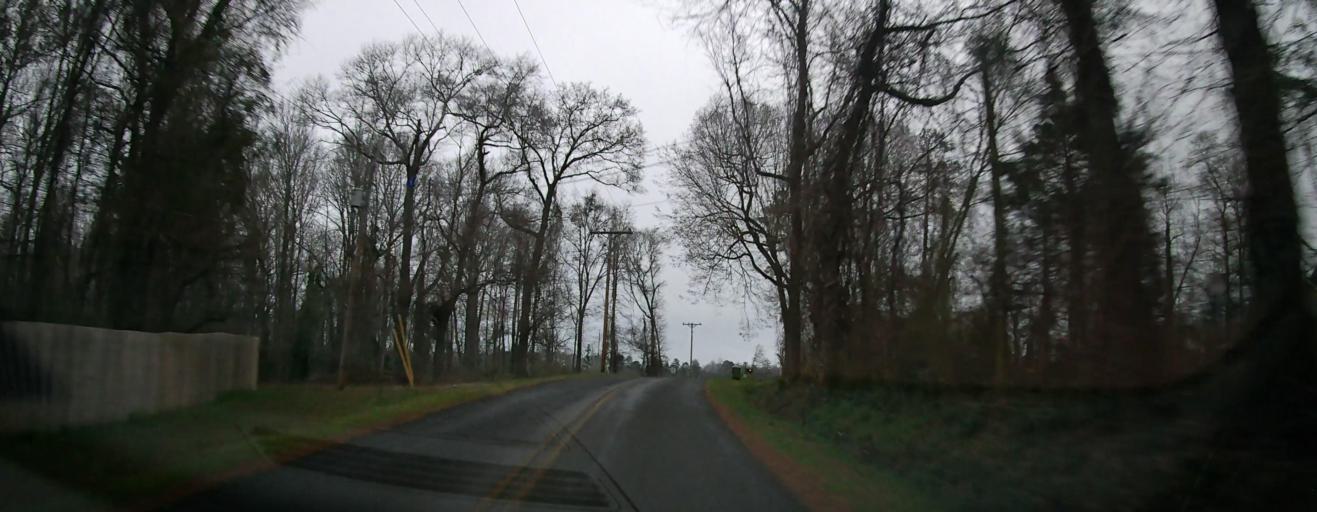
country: US
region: Georgia
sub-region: Bibb County
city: West Point
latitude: 32.9231
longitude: -83.7938
